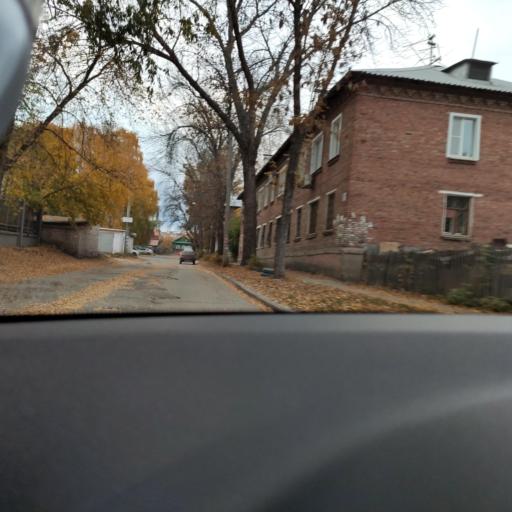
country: RU
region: Samara
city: Samara
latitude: 53.2281
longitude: 50.2355
